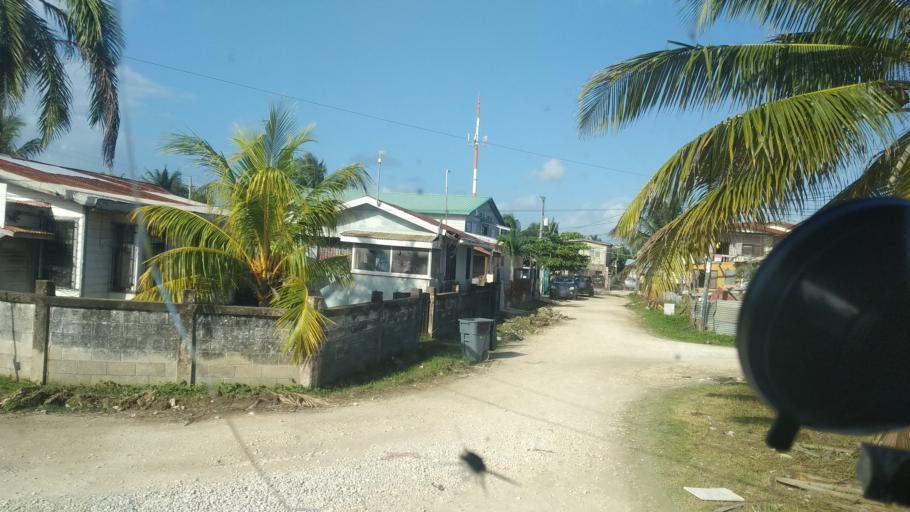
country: BZ
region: Belize
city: Belize City
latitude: 17.4852
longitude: -88.2039
